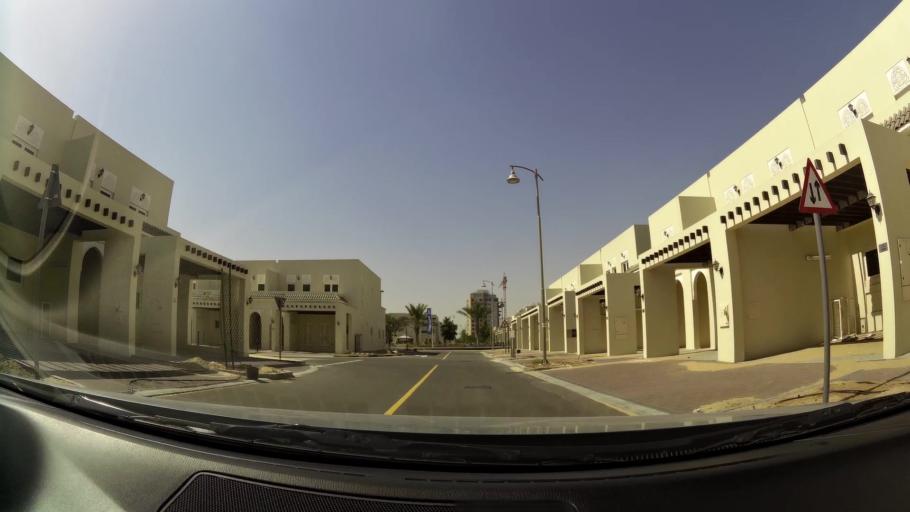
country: AE
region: Dubai
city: Dubai
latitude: 25.0235
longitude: 55.1486
